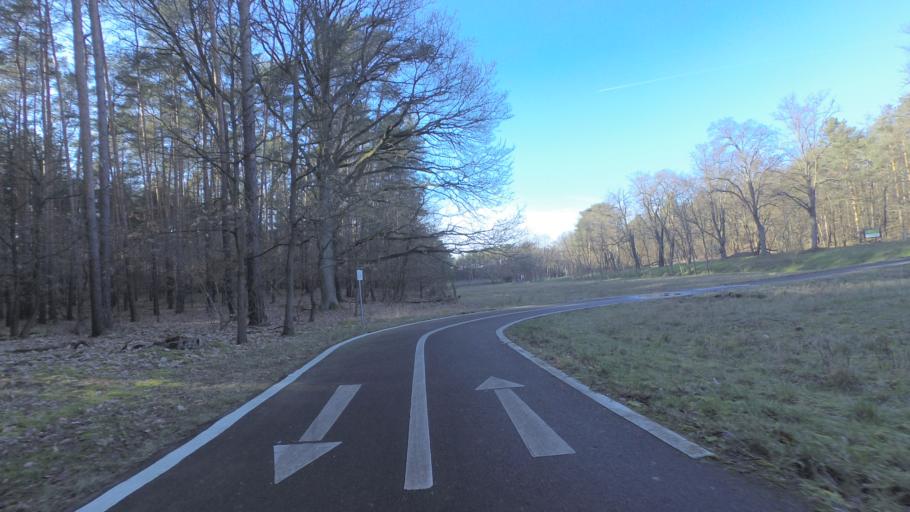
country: DE
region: Brandenburg
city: Ihlow
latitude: 52.0008
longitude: 13.3309
